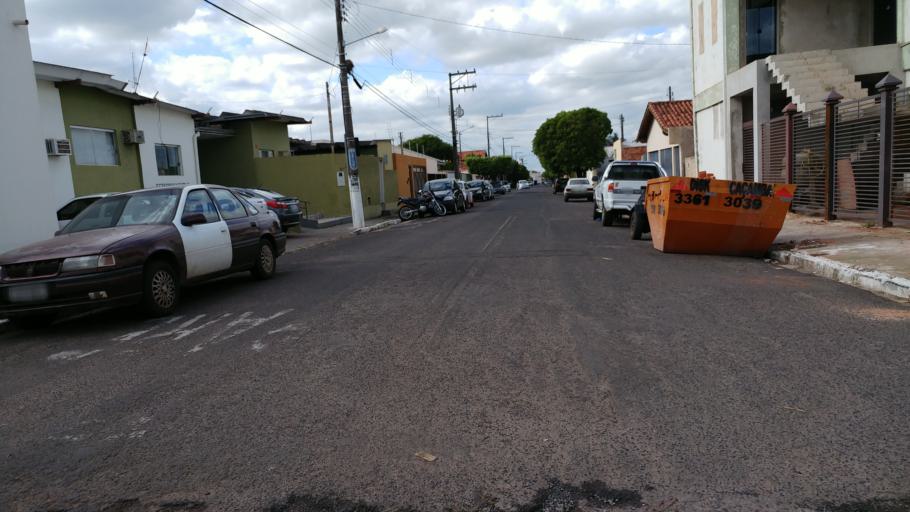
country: BR
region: Sao Paulo
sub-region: Paraguacu Paulista
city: Paraguacu Paulista
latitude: -22.4116
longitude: -50.5782
